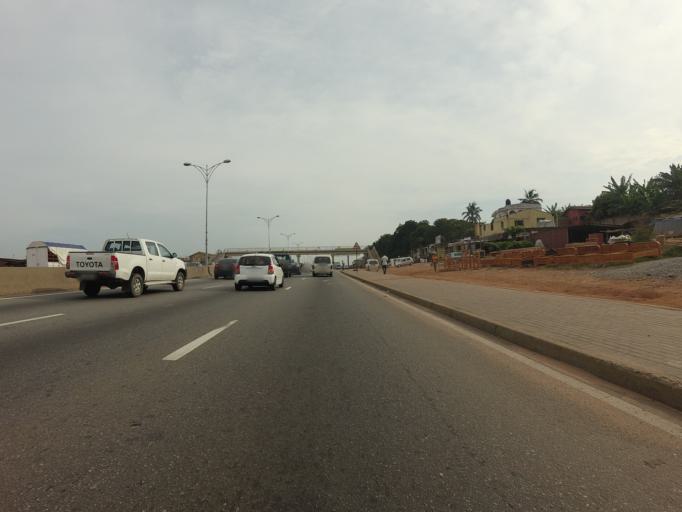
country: GH
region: Greater Accra
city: Gbawe
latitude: 5.5881
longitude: -0.2710
